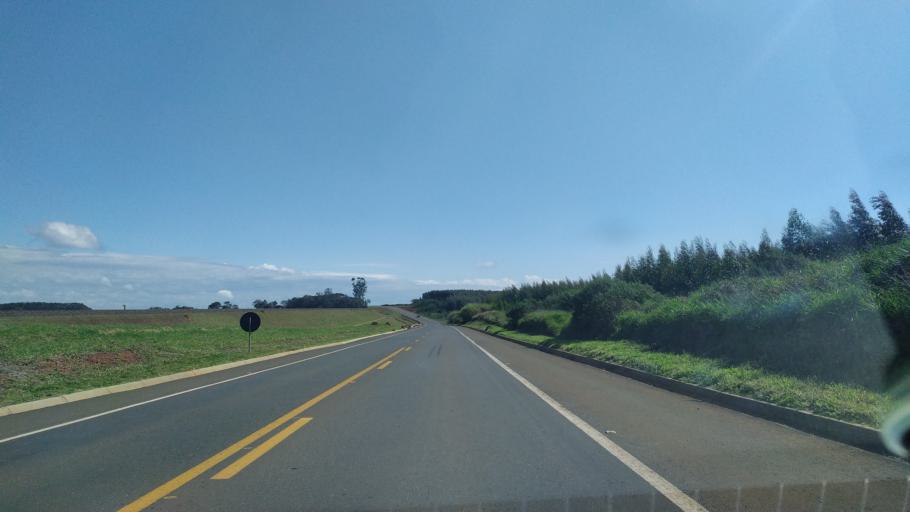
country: BR
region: Parana
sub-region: Ortigueira
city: Ortigueira
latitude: -24.2563
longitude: -50.7946
